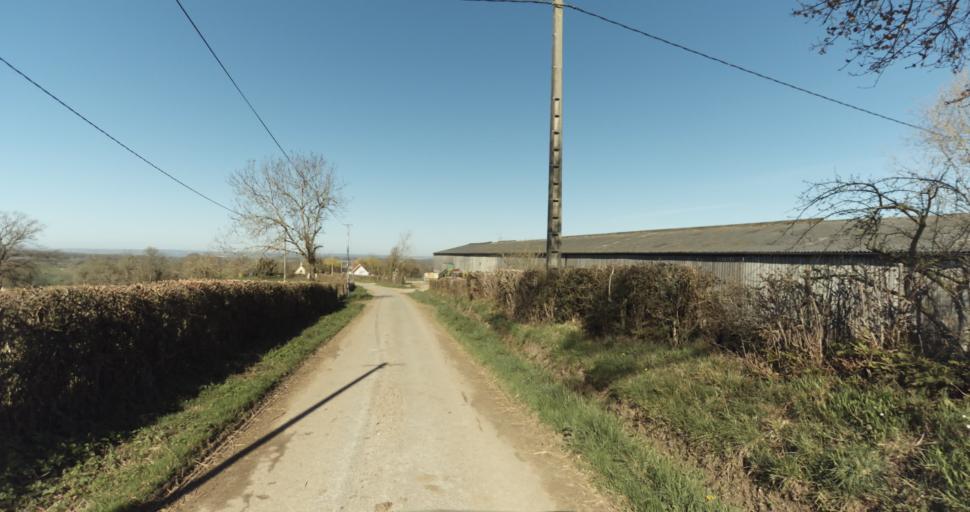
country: FR
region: Lower Normandy
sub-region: Departement de l'Orne
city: Trun
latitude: 48.9133
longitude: 0.0508
